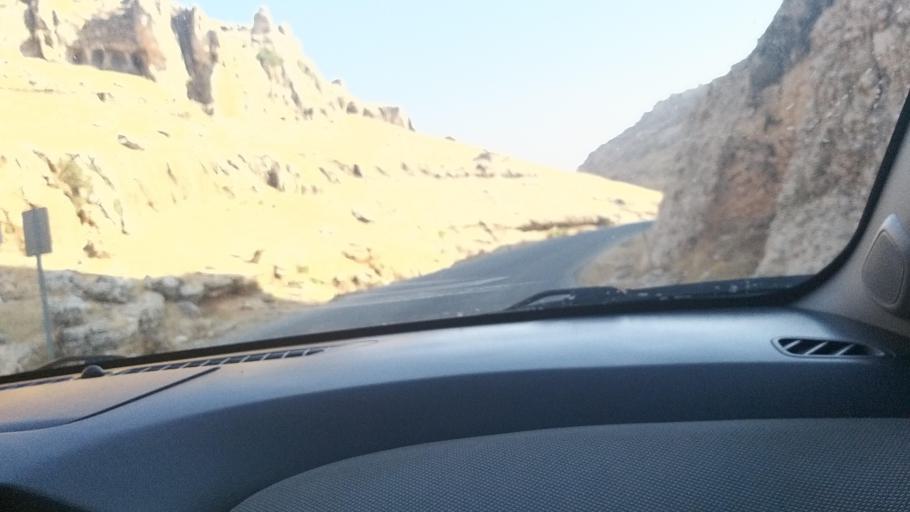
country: TR
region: Diyarbakir
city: Silvan
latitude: 38.1662
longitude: 41.0021
